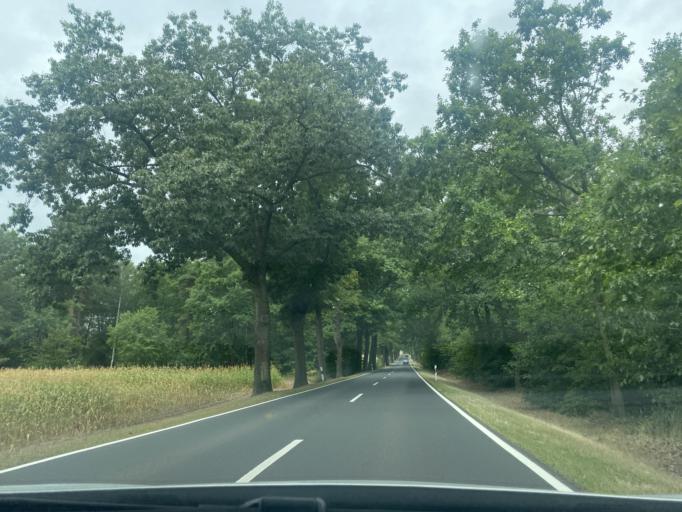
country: DE
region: Saxony
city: Mucka
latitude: 51.2816
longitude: 14.6499
